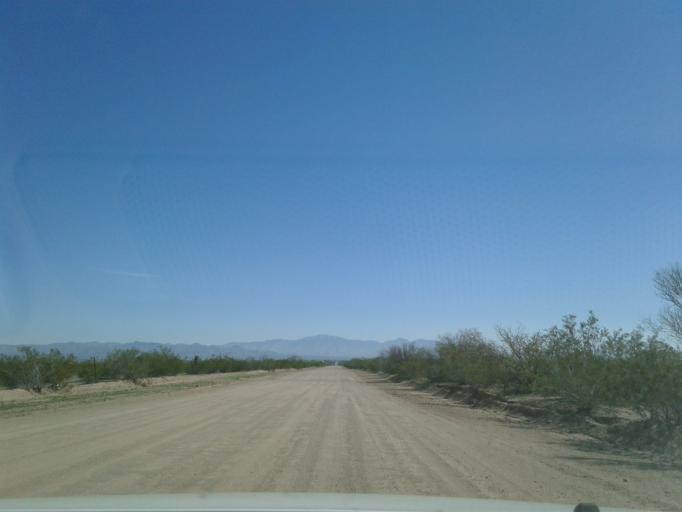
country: US
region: Arizona
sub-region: Pima County
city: Avra Valley
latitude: 32.4293
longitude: -111.3603
